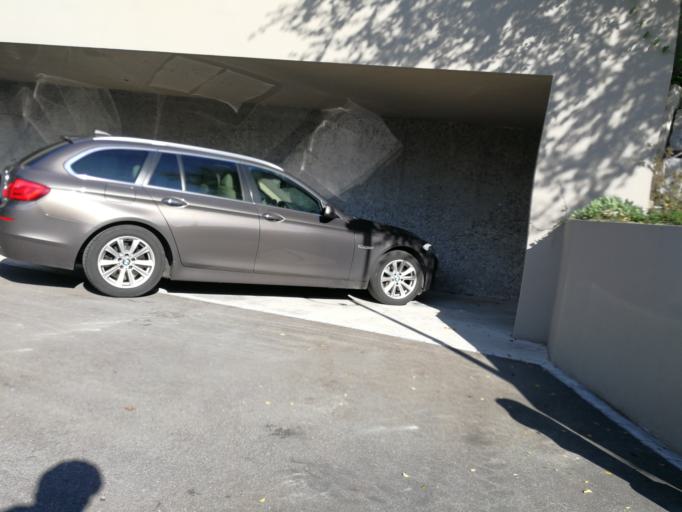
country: CH
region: Zurich
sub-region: Bezirk Meilen
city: Uerikon
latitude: 47.2383
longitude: 8.7619
